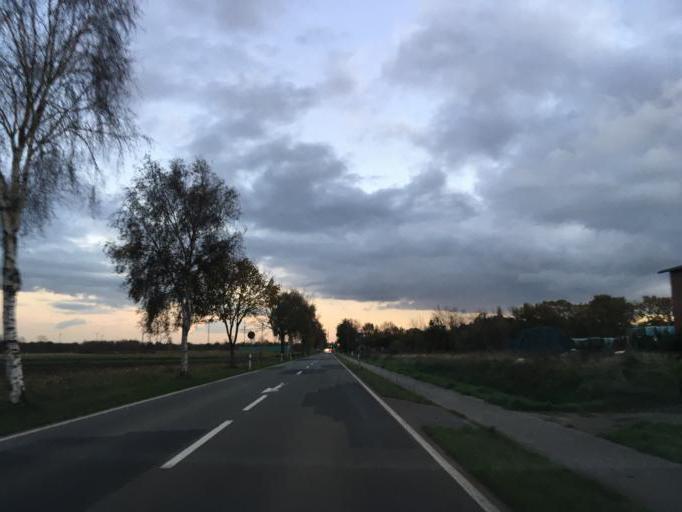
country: DE
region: Lower Saxony
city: Stelle
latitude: 53.3598
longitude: 10.1388
